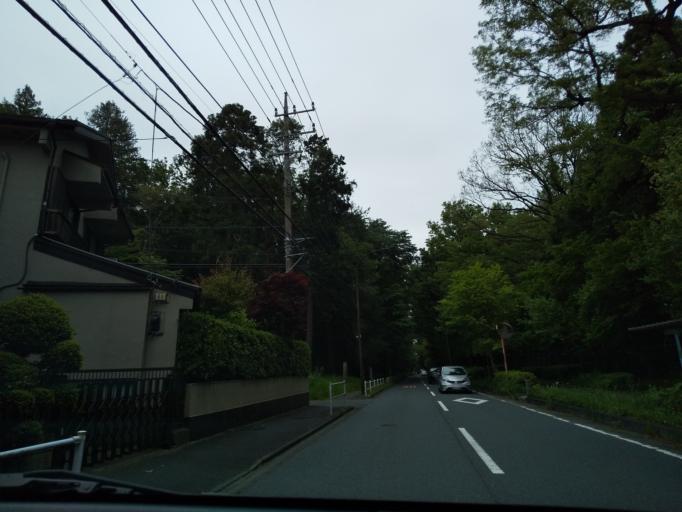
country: JP
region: Tokyo
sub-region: Machida-shi
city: Machida
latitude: 35.5425
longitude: 139.4058
